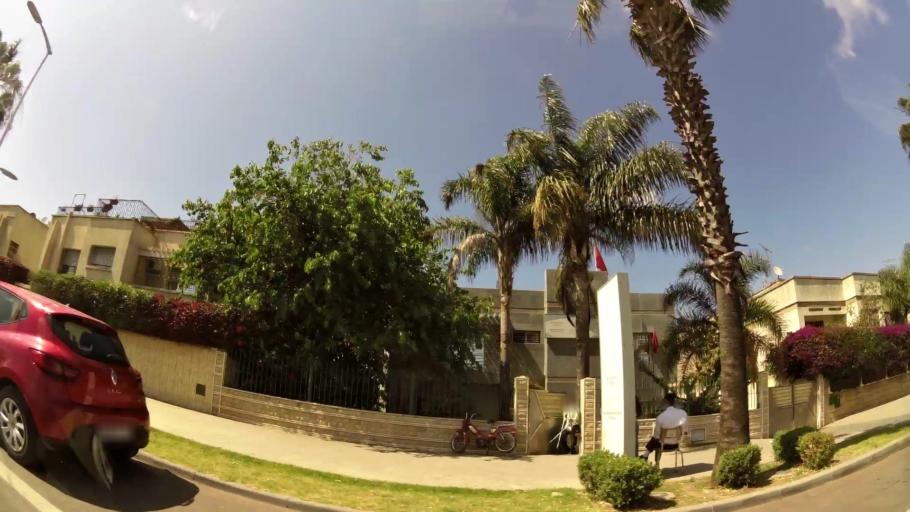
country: MA
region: Rabat-Sale-Zemmour-Zaer
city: Sale
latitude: 34.0352
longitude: -6.7904
